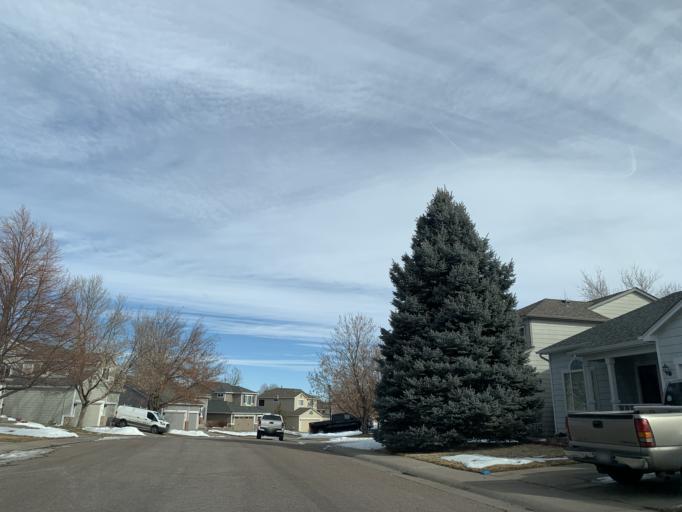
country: US
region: Colorado
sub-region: Douglas County
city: Carriage Club
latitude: 39.5395
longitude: -104.9248
